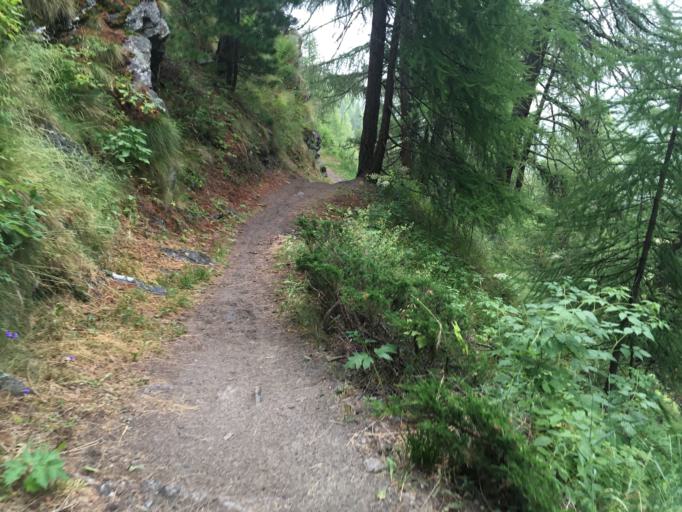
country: CH
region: Valais
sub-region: Visp District
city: Zermatt
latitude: 46.0087
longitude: 7.7278
